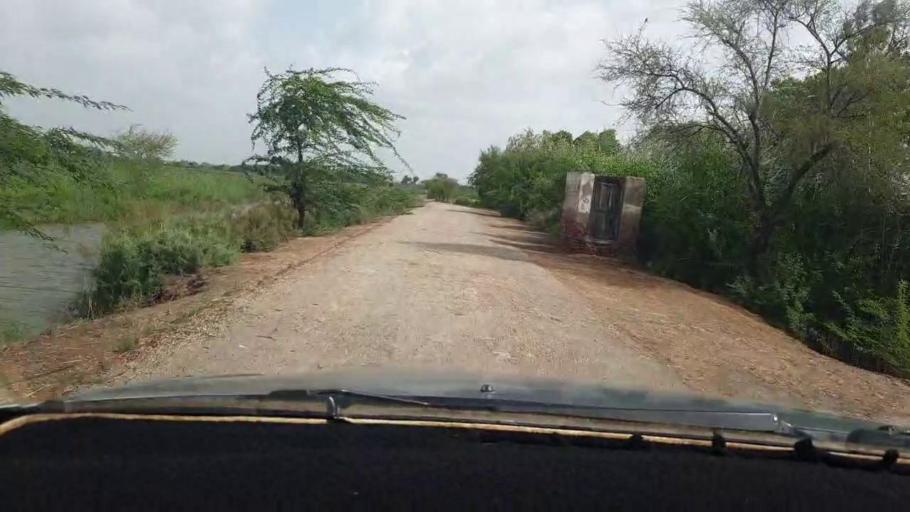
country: PK
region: Sindh
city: Tando Bago
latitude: 24.7896
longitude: 69.0286
